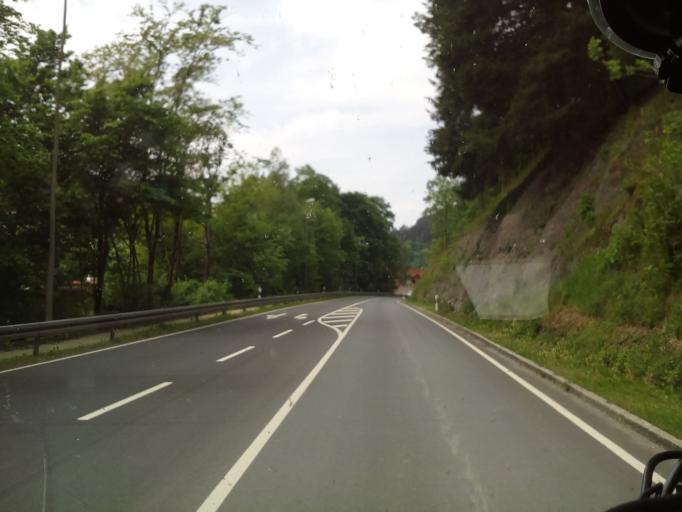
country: DE
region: Bavaria
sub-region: Upper Franconia
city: Steinwiesen
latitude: 50.2908
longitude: 11.4493
